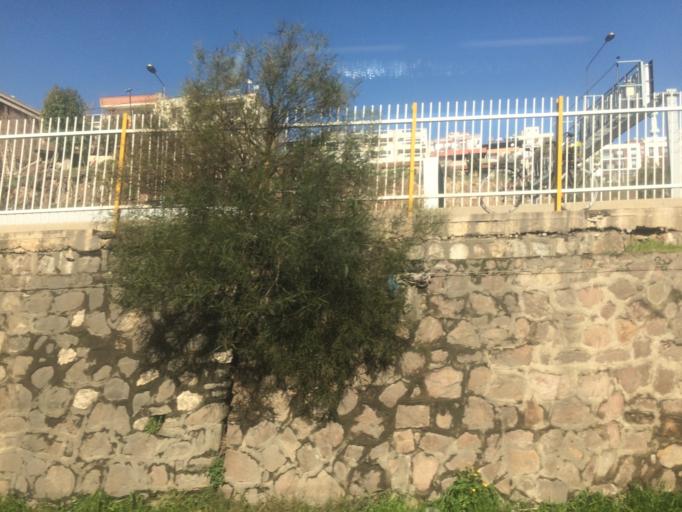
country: TR
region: Izmir
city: Karsiyaka
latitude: 38.4652
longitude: 27.1351
